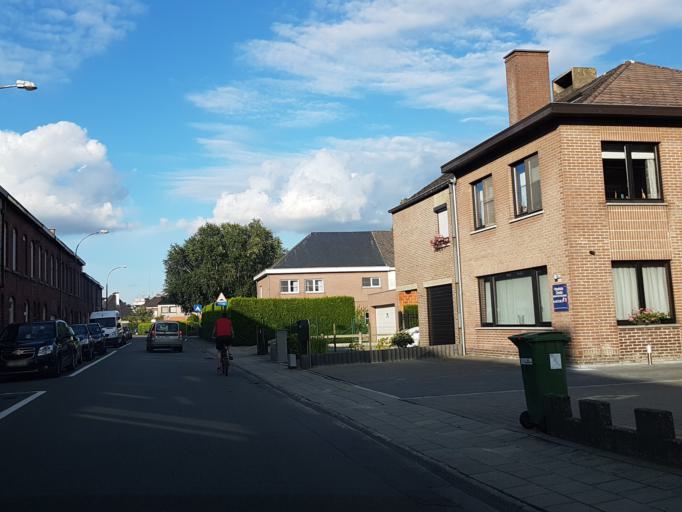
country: BE
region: Flanders
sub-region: Provincie Oost-Vlaanderen
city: Aalst
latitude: 50.9491
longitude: 4.0605
